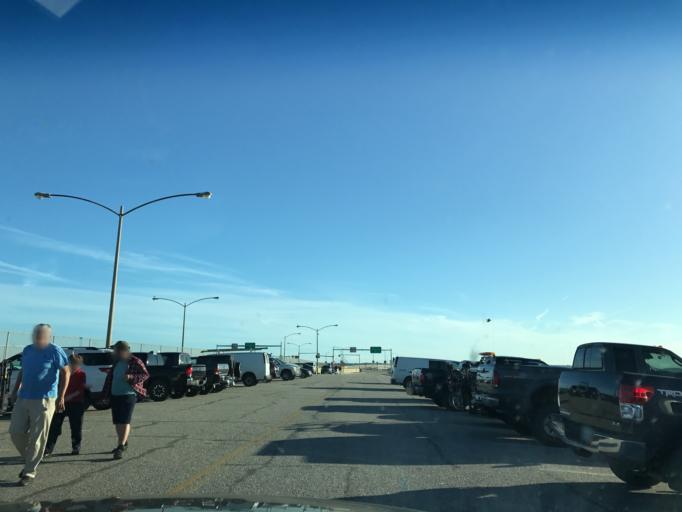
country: US
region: Virginia
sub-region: City of Virginia Beach
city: Virginia Beach
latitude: 36.9654
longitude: -76.1132
